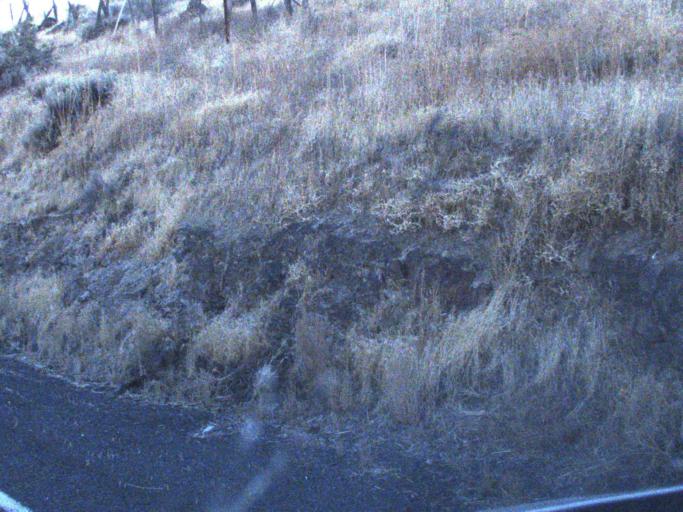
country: US
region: Washington
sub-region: Franklin County
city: Connell
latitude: 46.6536
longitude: -118.4979
